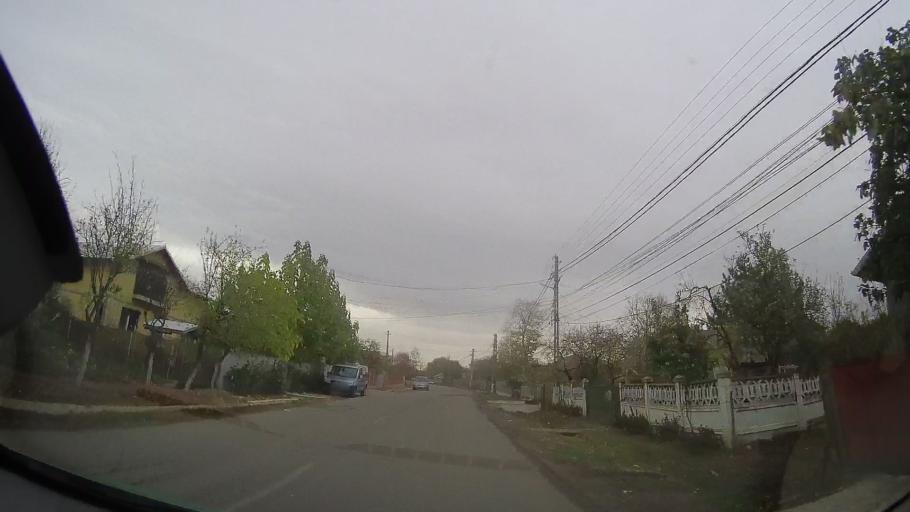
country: RO
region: Prahova
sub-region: Comuna Vadu Sapat
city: Vadu Sapat
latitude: 45.0318
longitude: 26.3854
